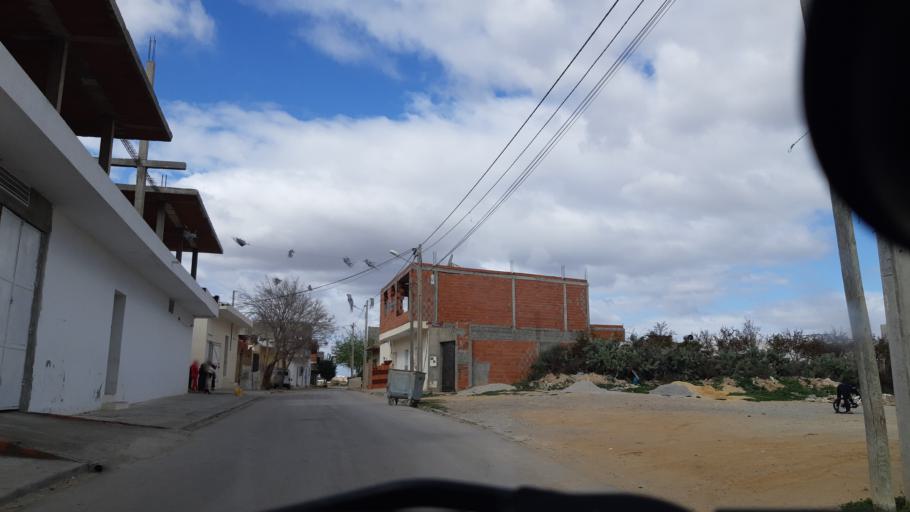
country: TN
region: Susah
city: Akouda
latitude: 35.8681
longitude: 10.5206
